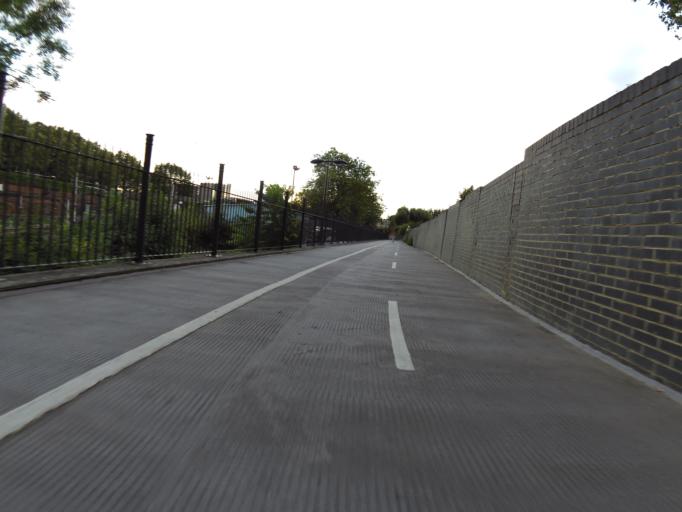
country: GB
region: England
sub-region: Greater London
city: Holloway
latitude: 51.5426
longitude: -0.1317
